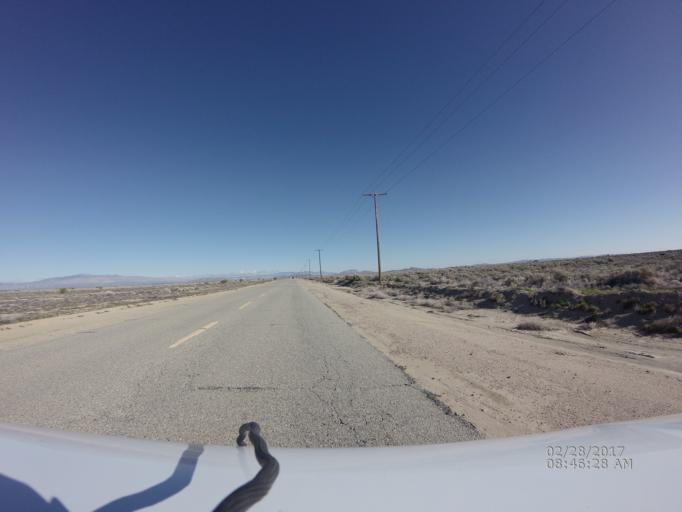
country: US
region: California
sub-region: Kern County
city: Rosamond
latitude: 34.7703
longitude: -118.2373
